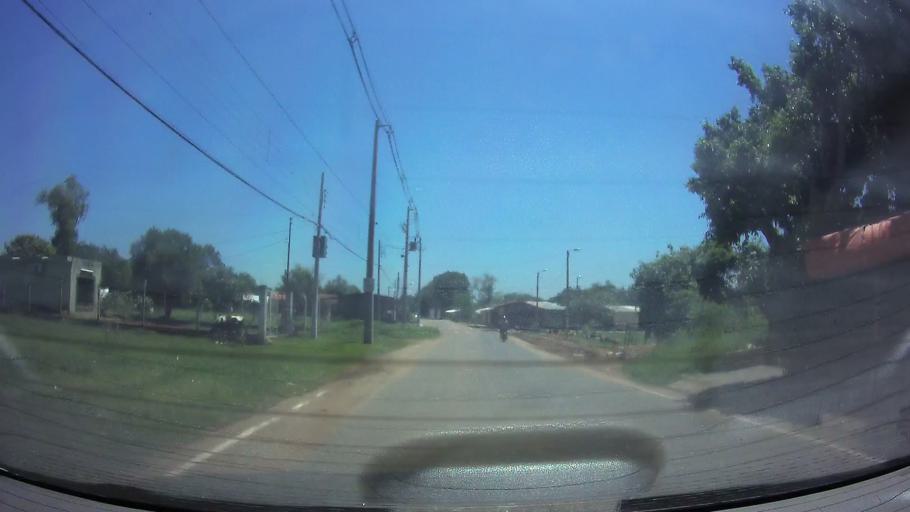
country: PY
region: Central
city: San Lorenzo
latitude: -25.3250
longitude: -57.4834
